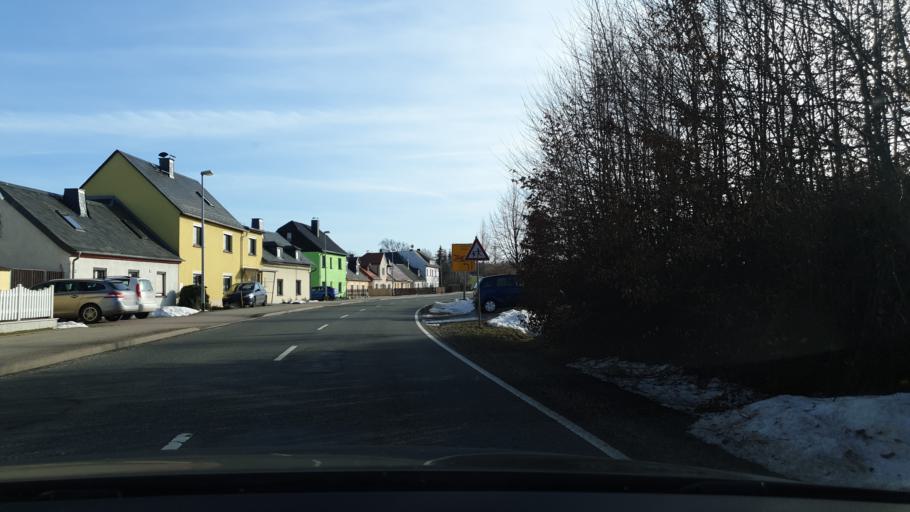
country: DE
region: Thuringia
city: Hohenleuben
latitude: 50.6903
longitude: 12.0538
